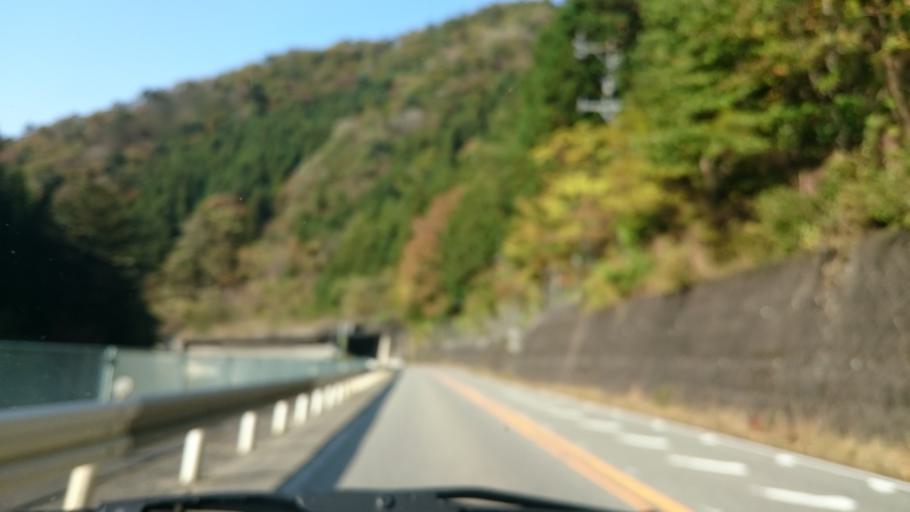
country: JP
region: Gifu
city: Gujo
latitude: 35.7697
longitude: 137.2594
